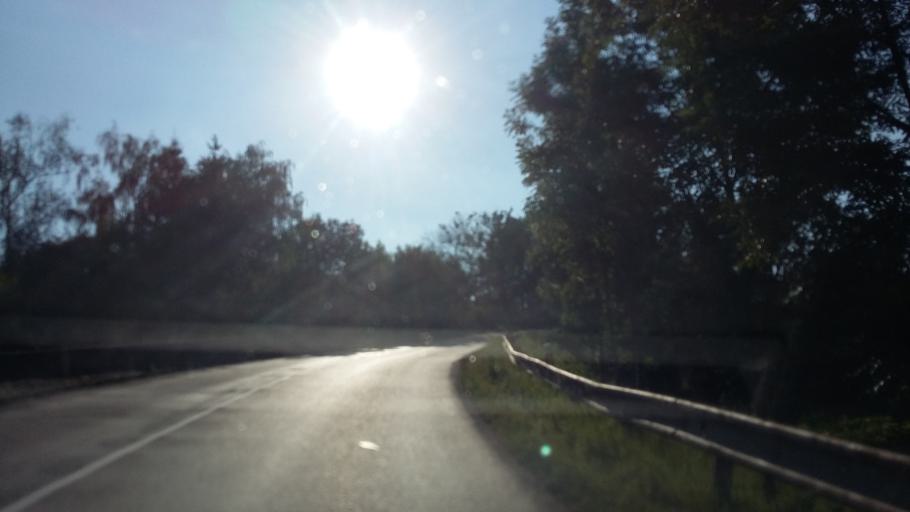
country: CZ
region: South Moravian
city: Ricany
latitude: 49.2154
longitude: 16.3856
